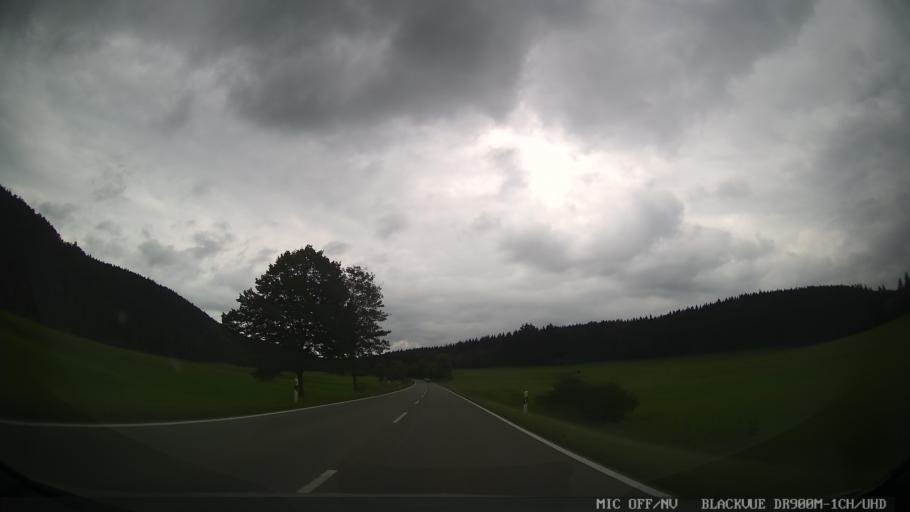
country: DE
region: Baden-Wuerttemberg
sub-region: Freiburg Region
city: Fridingen an der Donau
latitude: 48.0014
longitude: 8.9208
